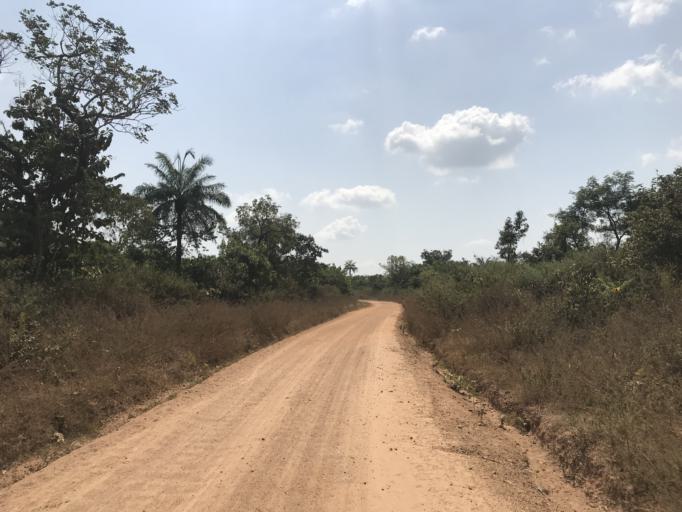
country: NG
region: Osun
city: Ifon
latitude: 7.9486
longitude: 4.4930
